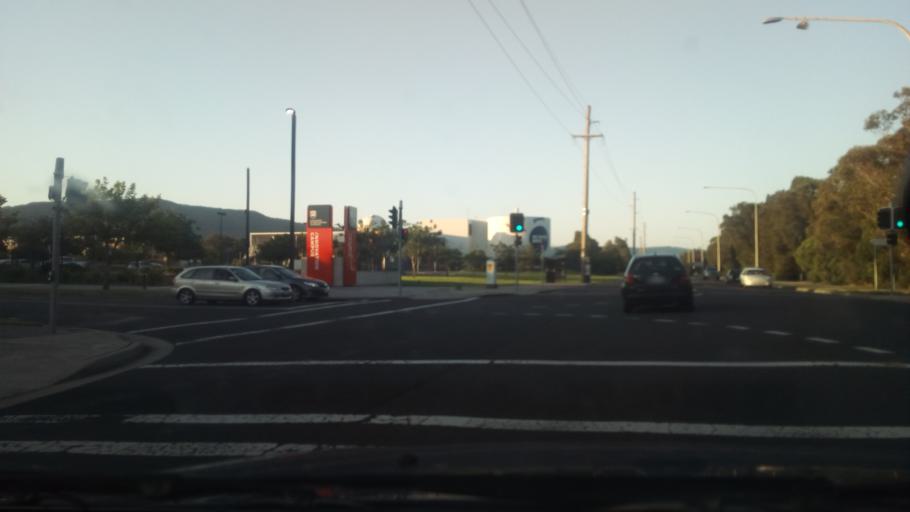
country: AU
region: New South Wales
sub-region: Wollongong
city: Fairy Meadow
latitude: -34.4025
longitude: 150.9002
